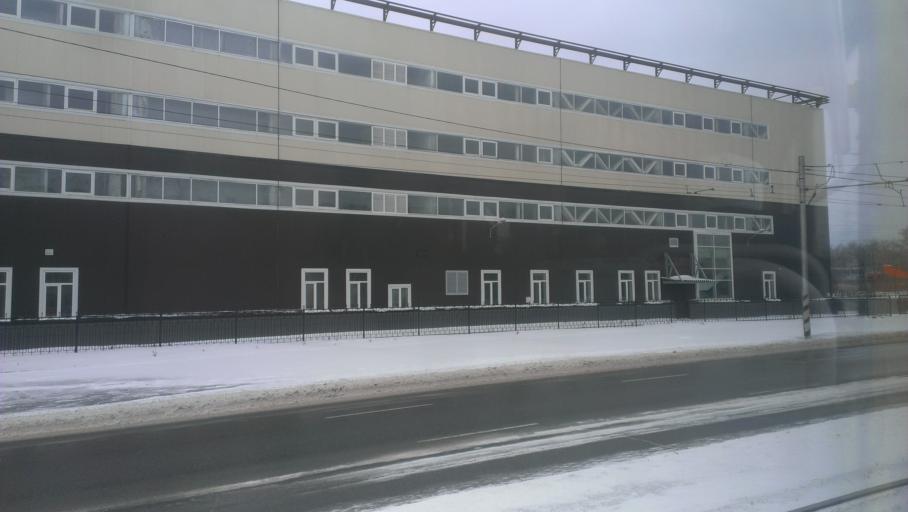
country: RU
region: Altai Krai
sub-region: Gorod Barnaulskiy
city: Barnaul
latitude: 53.3842
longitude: 83.7130
